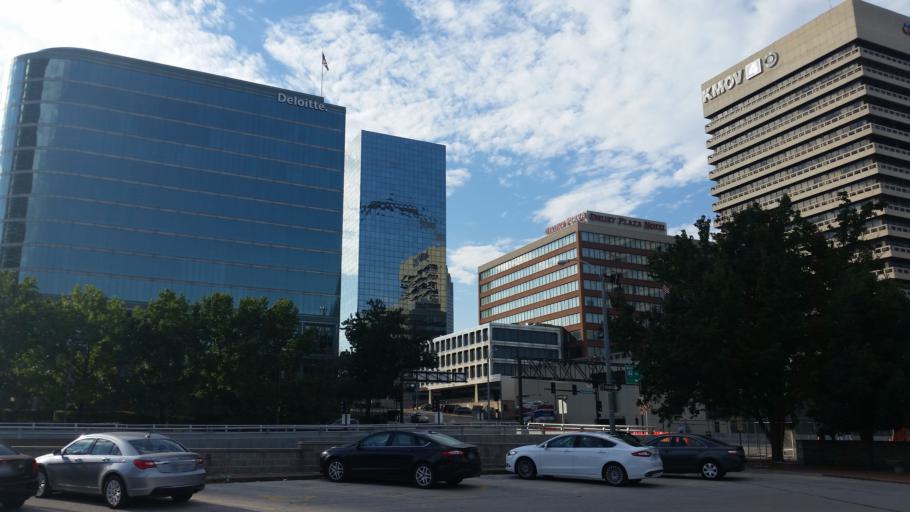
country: US
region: Missouri
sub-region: City of Saint Louis
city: St. Louis
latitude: 38.6234
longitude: -90.1872
